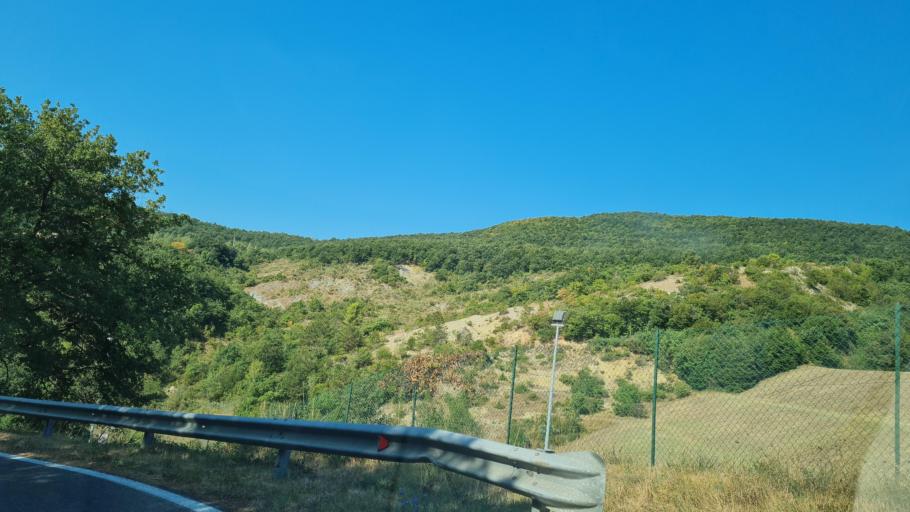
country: IT
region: Tuscany
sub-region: Provincia di Siena
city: Chianciano Terme
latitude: 43.0347
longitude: 11.7962
